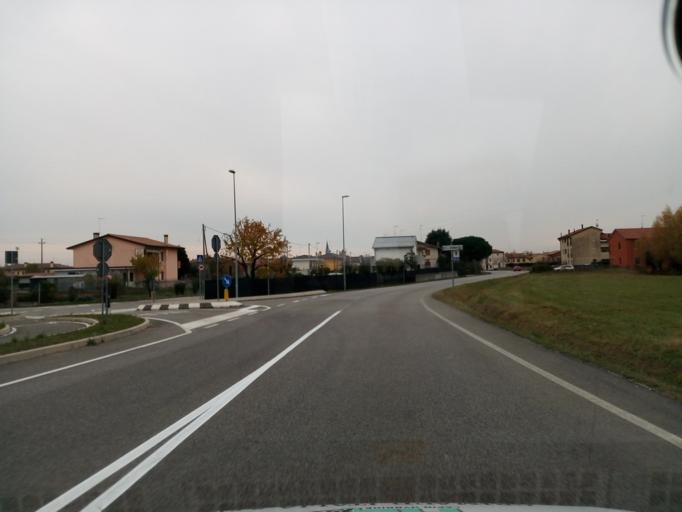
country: IT
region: Veneto
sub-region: Provincia di Treviso
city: Vedelago
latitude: 45.6925
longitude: 12.0172
